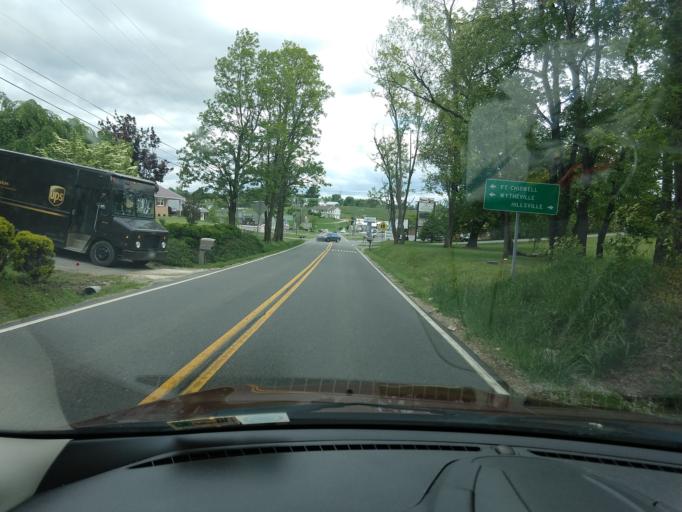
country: US
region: Virginia
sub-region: Wythe County
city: Wytheville
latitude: 36.9280
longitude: -80.9420
